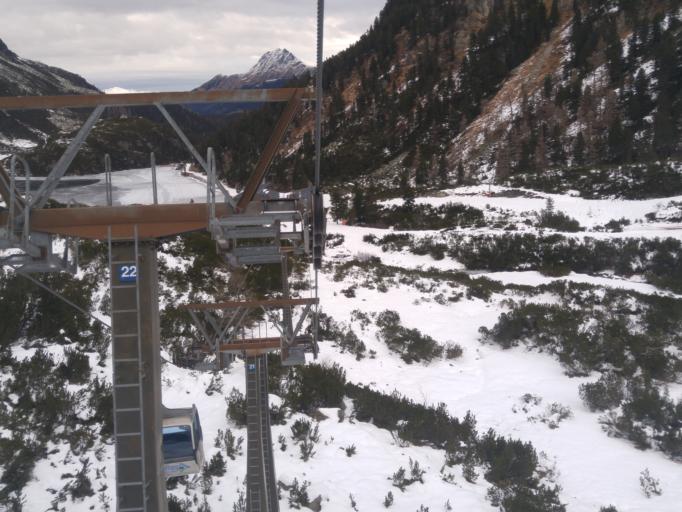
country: AT
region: Salzburg
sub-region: Politischer Bezirk Zell am See
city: Niedernsill
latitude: 47.1539
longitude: 12.6242
